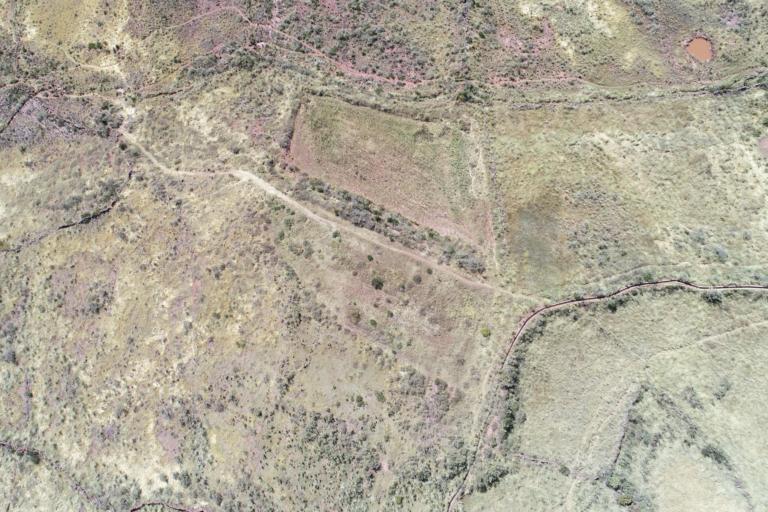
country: BO
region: La Paz
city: Tiahuanaco
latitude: -16.6094
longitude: -68.7658
